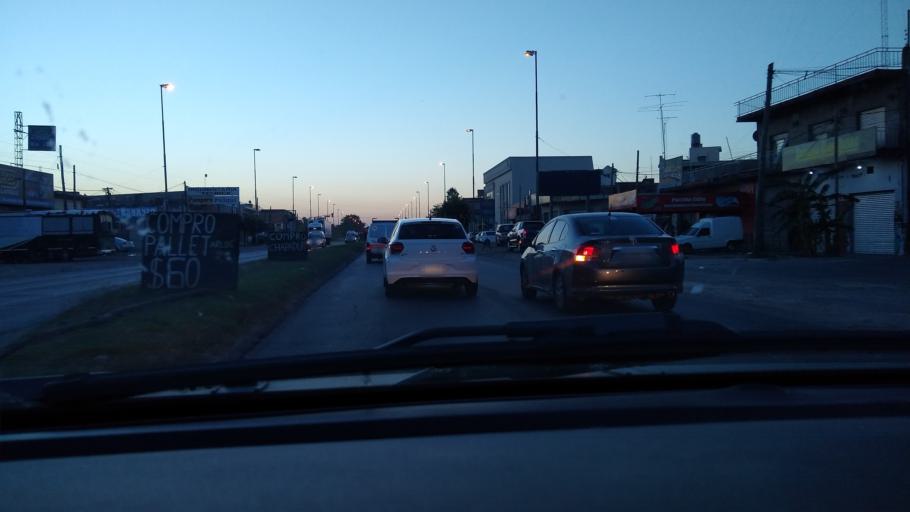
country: AR
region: Buenos Aires
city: San Justo
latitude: -34.6816
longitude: -58.5758
